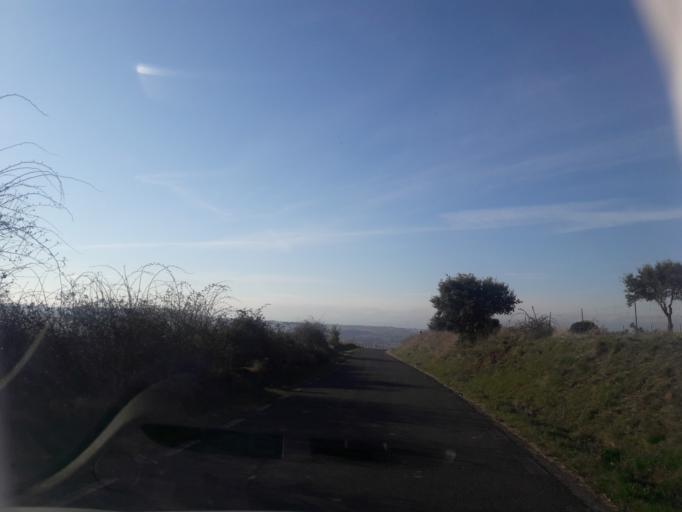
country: ES
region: Castille and Leon
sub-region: Provincia de Salamanca
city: Salvatierra de Tormes
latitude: 40.6050
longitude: -5.6009
